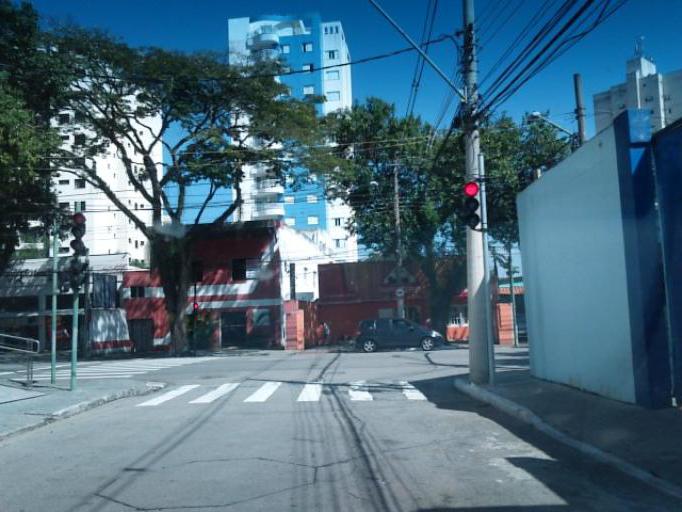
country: BR
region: Sao Paulo
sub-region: Sao Jose Dos Campos
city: Sao Jose dos Campos
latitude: -23.1937
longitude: -45.8930
